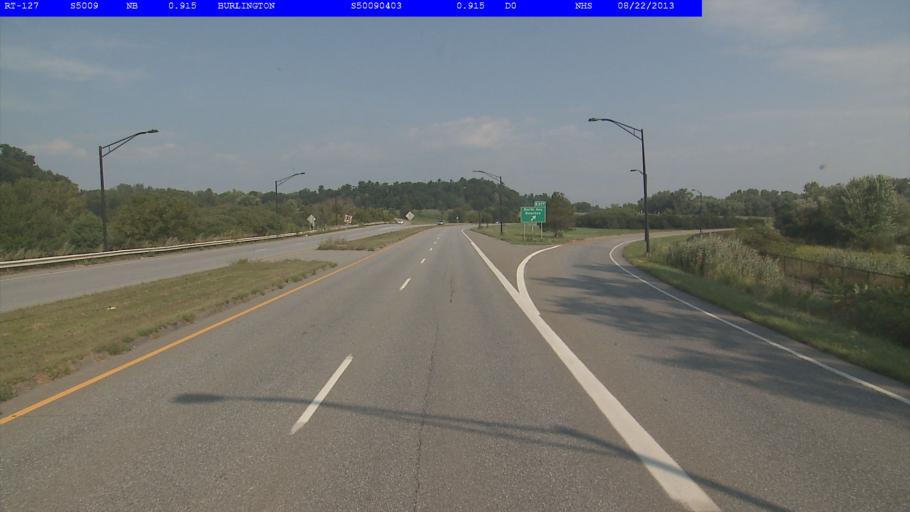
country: US
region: Vermont
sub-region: Chittenden County
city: Burlington
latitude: 44.4986
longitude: -73.2288
